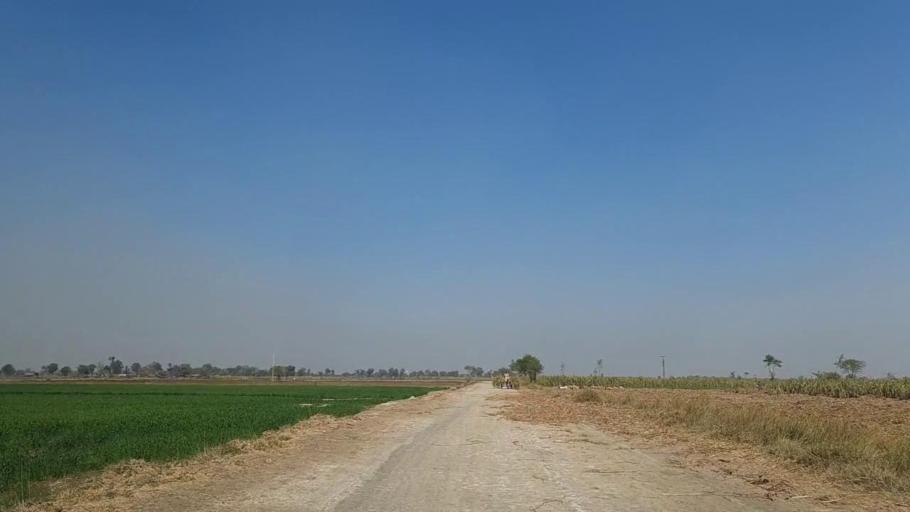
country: PK
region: Sindh
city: Daur
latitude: 26.4800
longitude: 68.3253
